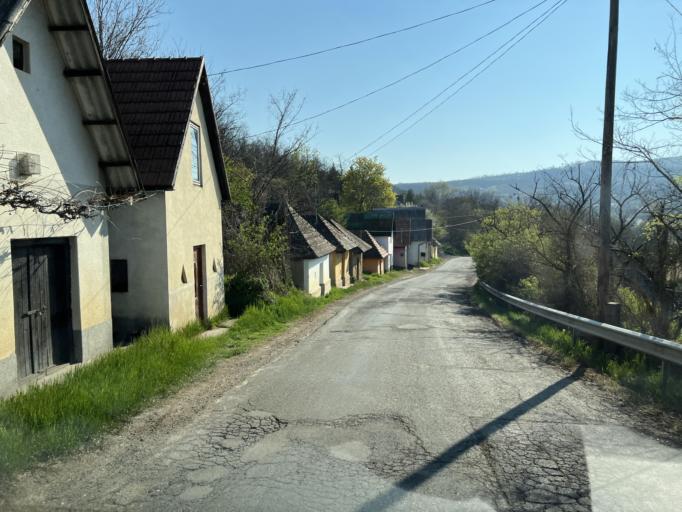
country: SK
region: Nitriansky
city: Sahy
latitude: 47.9987
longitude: 18.8559
